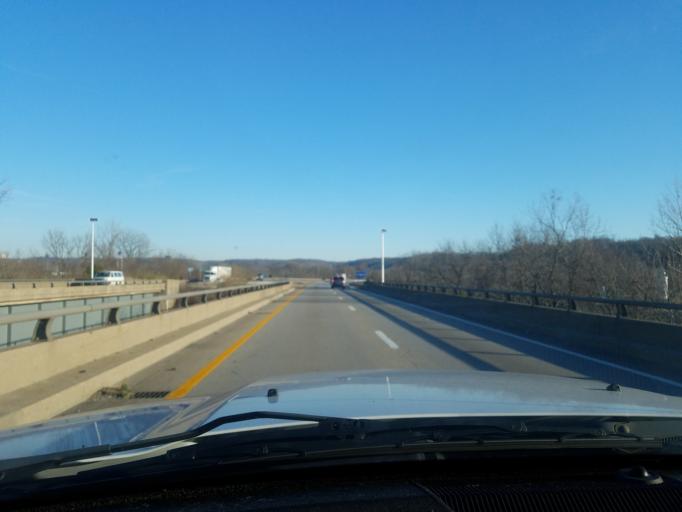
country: US
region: Kentucky
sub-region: Carroll County
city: Carrollton
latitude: 38.6431
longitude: -85.1248
